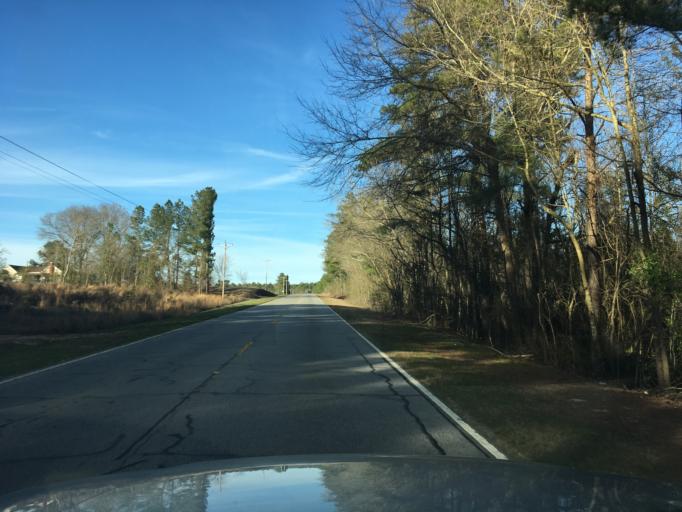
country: US
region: South Carolina
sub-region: Edgefield County
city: Johnston
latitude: 33.7380
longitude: -81.6475
